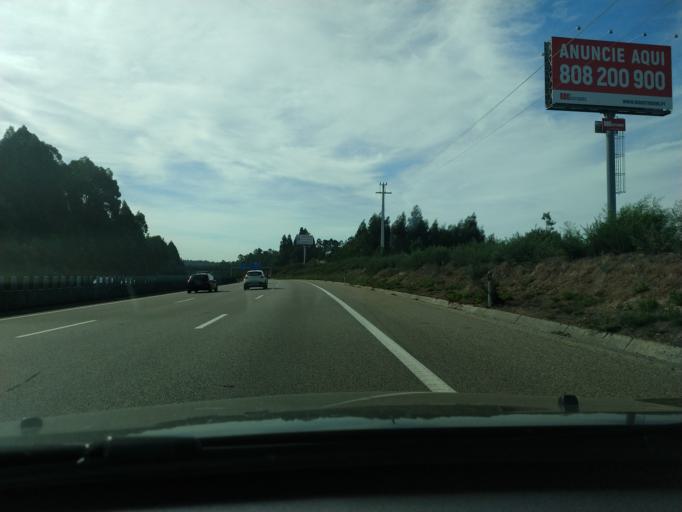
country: PT
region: Aveiro
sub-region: Santa Maria da Feira
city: Rio Meao
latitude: 40.9453
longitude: -8.5743
